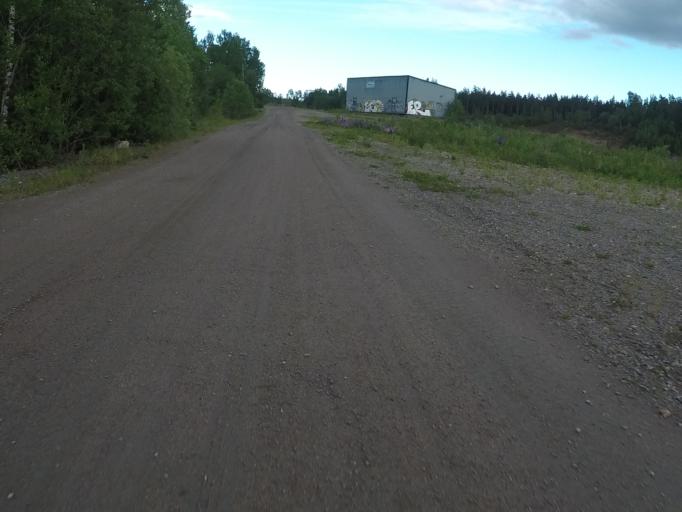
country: SE
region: Soedermanland
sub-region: Eskilstuna Kommun
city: Hallbybrunn
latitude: 59.4042
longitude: 16.4008
